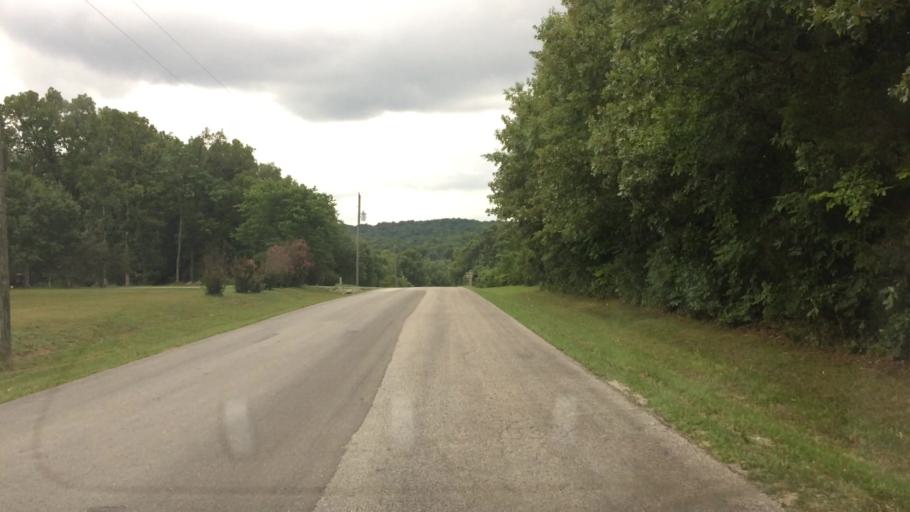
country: US
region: Missouri
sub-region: Webster County
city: Marshfield
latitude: 37.3083
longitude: -92.9846
